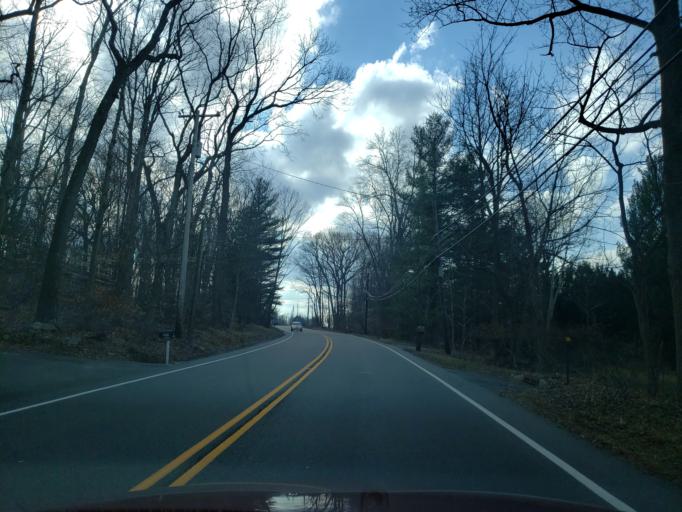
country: US
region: New Jersey
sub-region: Hunterdon County
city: Flemington
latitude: 40.4687
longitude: -74.9187
